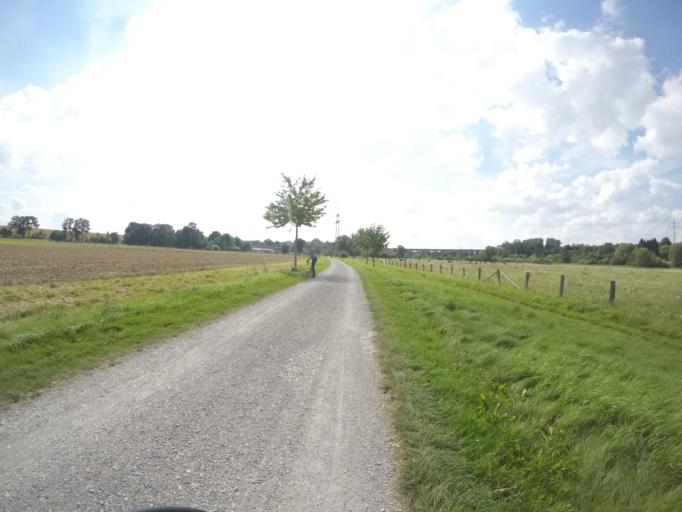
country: DE
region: North Rhine-Westphalia
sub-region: Regierungsbezirk Detmold
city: Bielefeld
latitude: 52.0539
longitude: 8.5790
